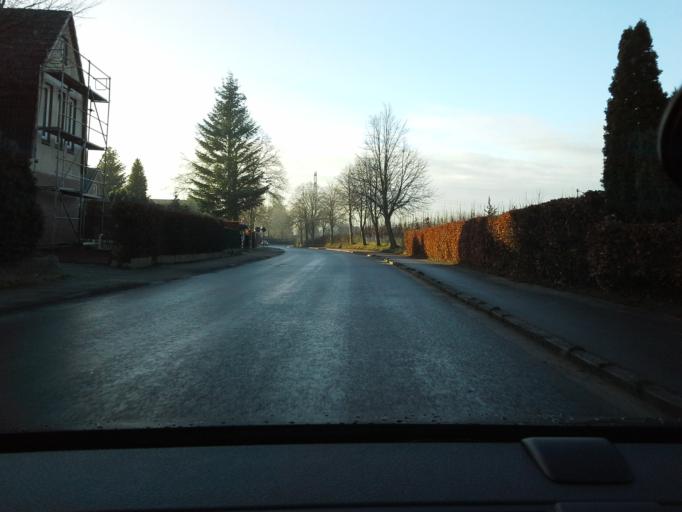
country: DE
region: Schleswig-Holstein
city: Borstel-Hohenraden
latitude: 53.6837
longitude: 9.8058
